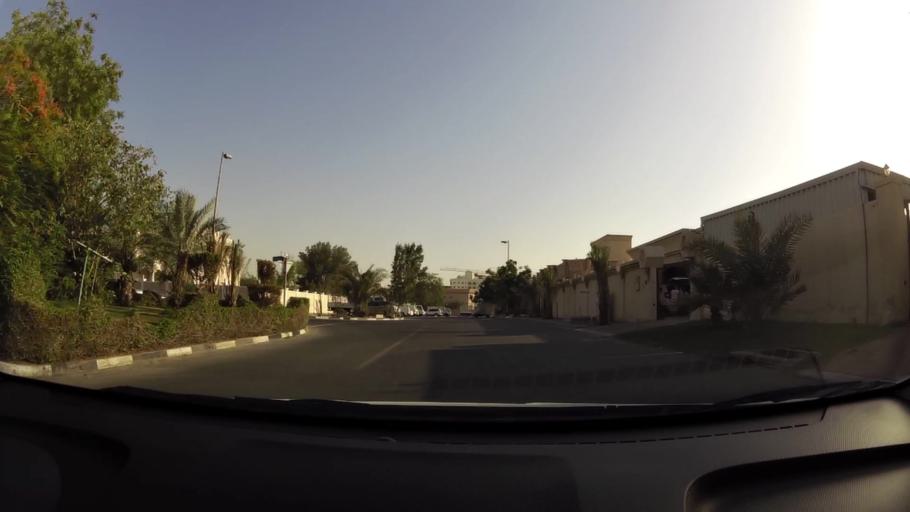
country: AE
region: Ash Shariqah
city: Sharjah
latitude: 25.2700
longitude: 55.3838
